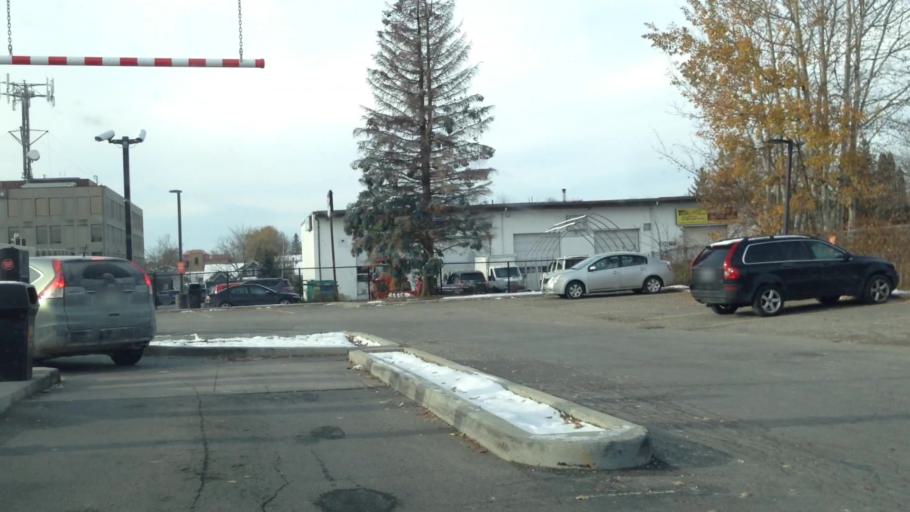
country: CA
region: Quebec
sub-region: Outaouais
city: Gatineau
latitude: 45.4720
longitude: -75.5244
